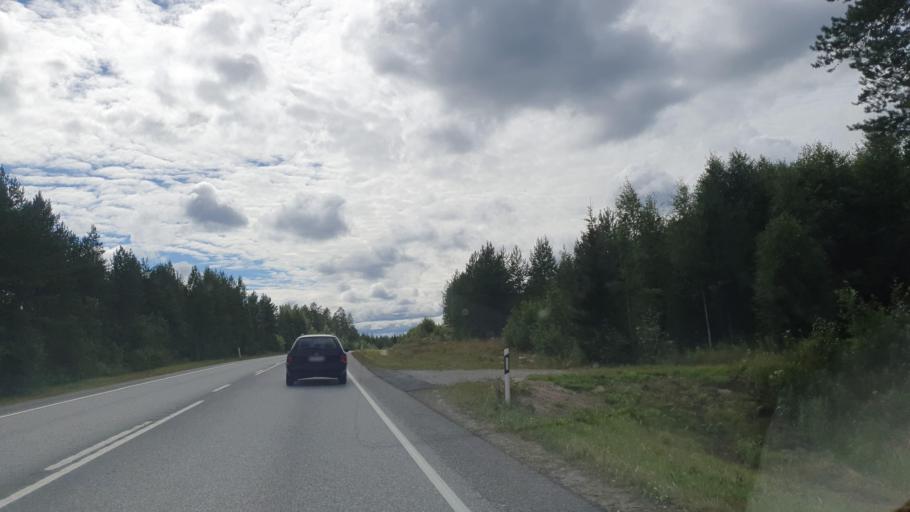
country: FI
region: Kainuu
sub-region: Kajaani
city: Kajaani
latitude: 64.1963
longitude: 27.6278
